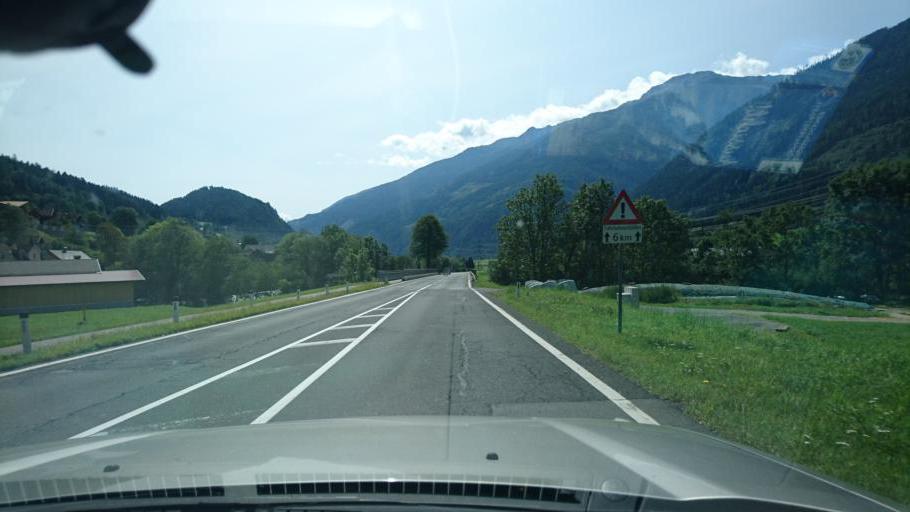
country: AT
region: Carinthia
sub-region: Politischer Bezirk Spittal an der Drau
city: Obervellach
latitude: 46.9039
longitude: 13.2577
